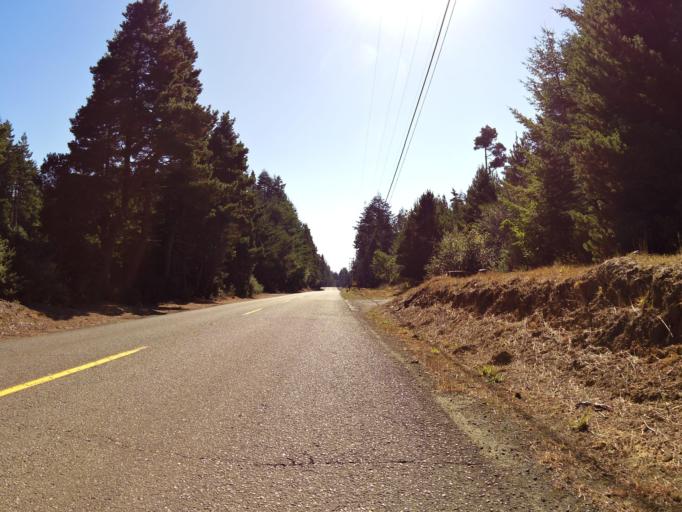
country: US
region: Oregon
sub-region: Coos County
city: Bandon
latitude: 43.1765
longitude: -124.3714
